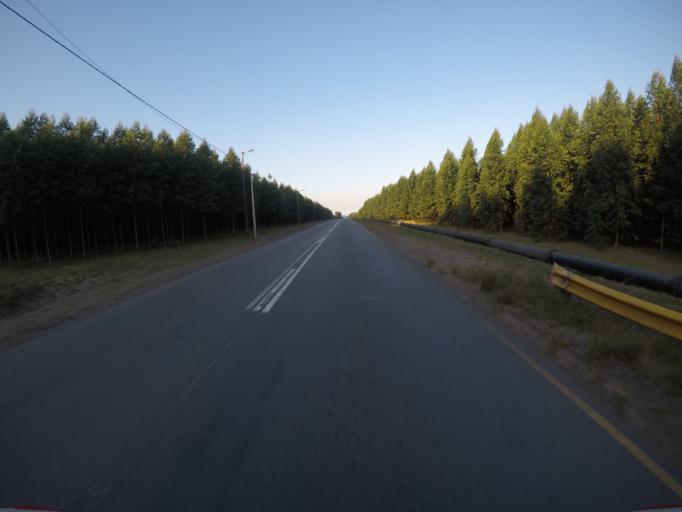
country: ZA
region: KwaZulu-Natal
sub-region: uThungulu District Municipality
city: KwaMbonambi
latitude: -28.6833
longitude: 32.1569
